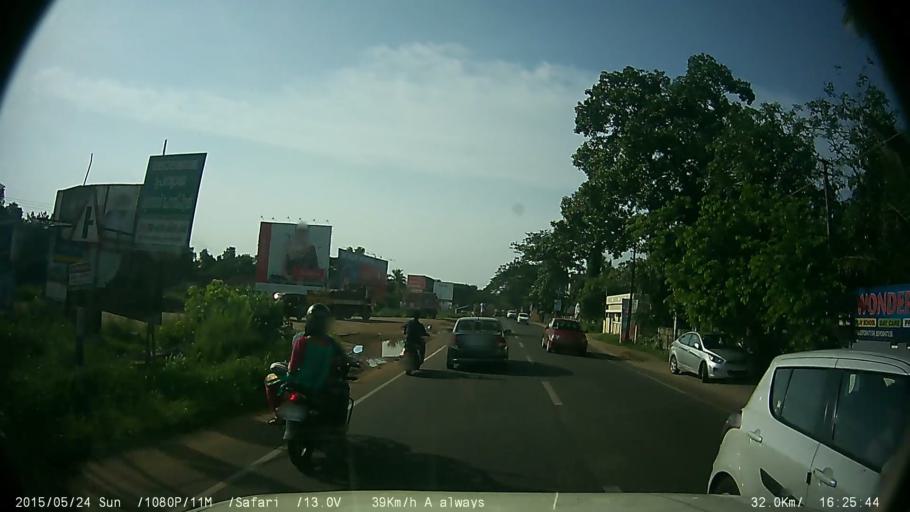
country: IN
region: Kerala
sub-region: Alappuzha
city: Alleppey
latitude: 9.5147
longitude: 76.3279
